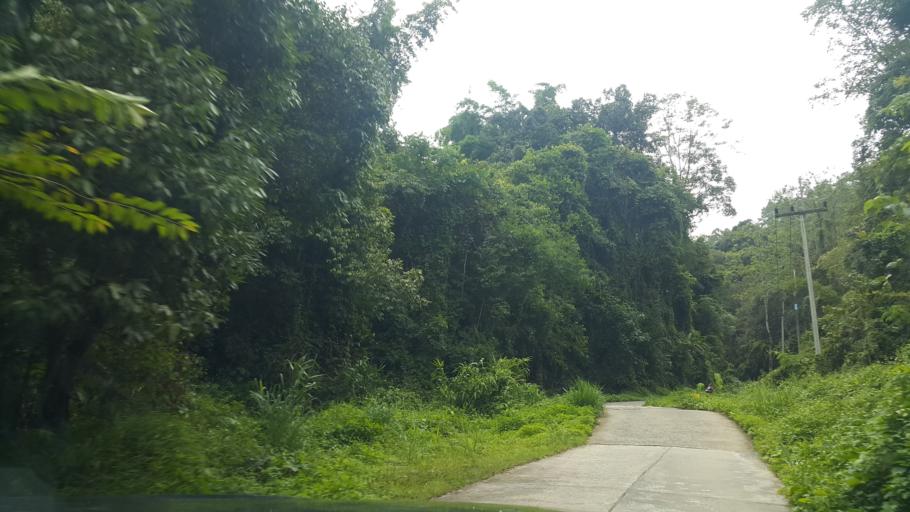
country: TH
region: Lampang
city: Wang Nuea
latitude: 19.0817
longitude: 99.3845
